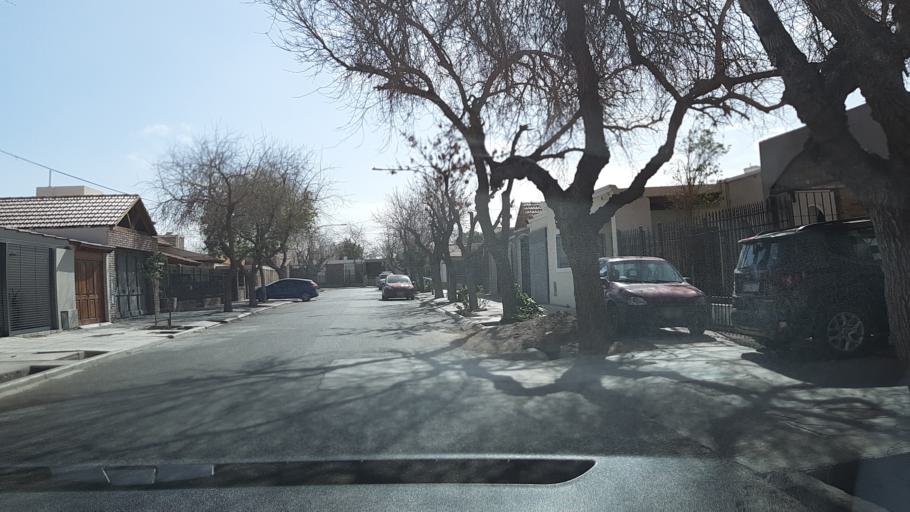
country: AR
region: San Juan
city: San Juan
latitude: -31.5272
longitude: -68.5464
